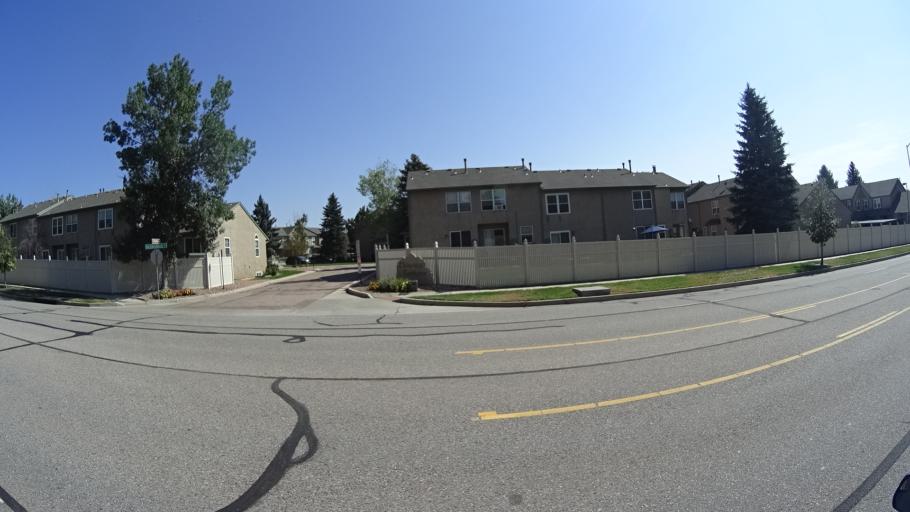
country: US
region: Colorado
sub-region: El Paso County
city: Air Force Academy
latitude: 38.9199
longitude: -104.8265
